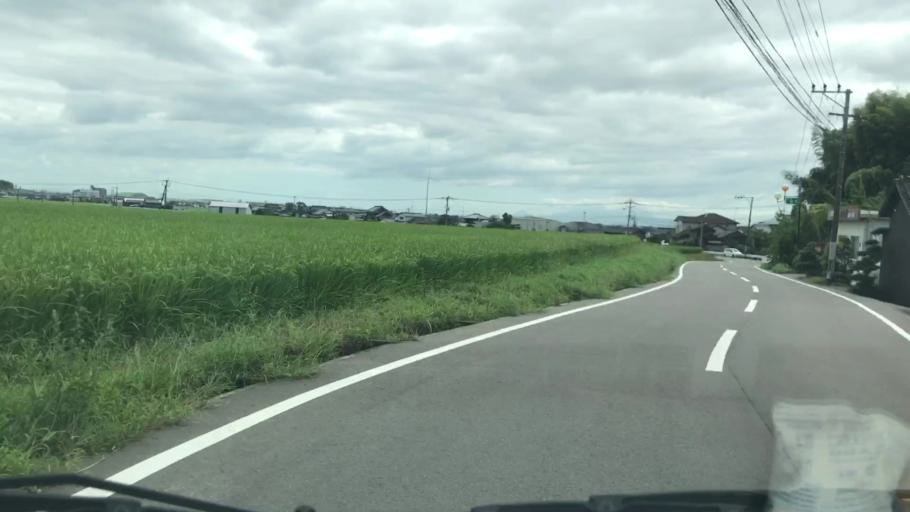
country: JP
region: Saga Prefecture
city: Takeocho-takeo
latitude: 33.2308
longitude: 130.1448
